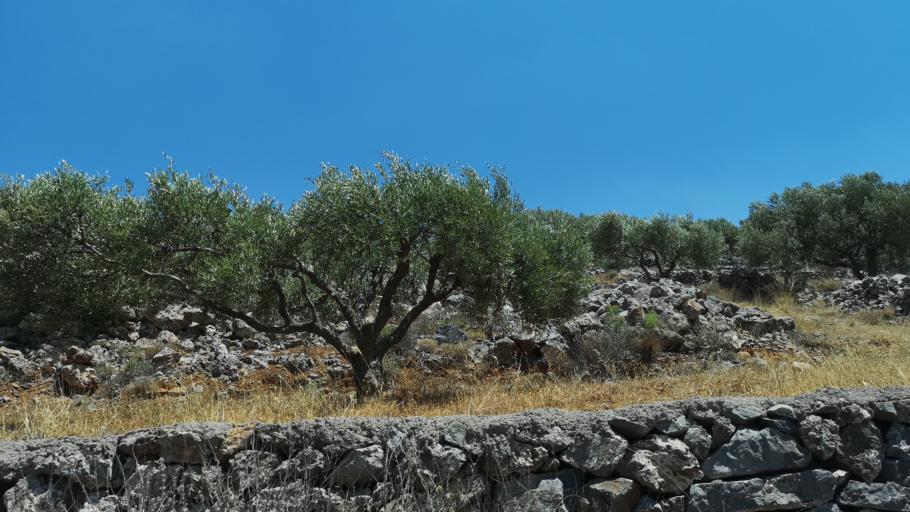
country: GR
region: Crete
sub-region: Nomos Lasithiou
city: Neapoli
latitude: 35.2560
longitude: 25.6406
